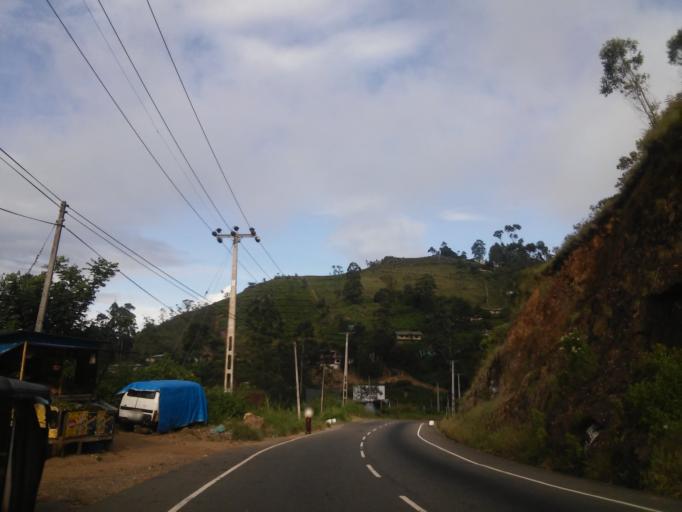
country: LK
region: Uva
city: Haputale
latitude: 6.7655
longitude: 80.9551
